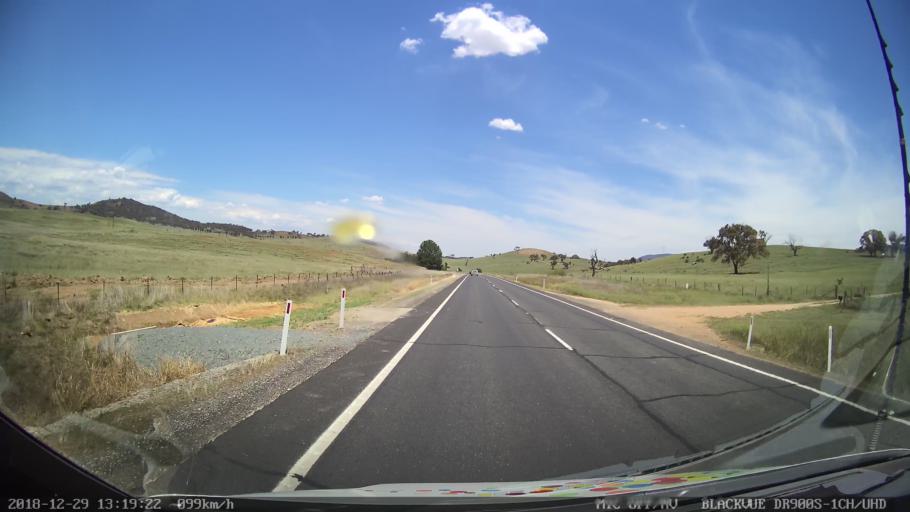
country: AU
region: Australian Capital Territory
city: Macarthur
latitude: -35.7643
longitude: 149.1614
